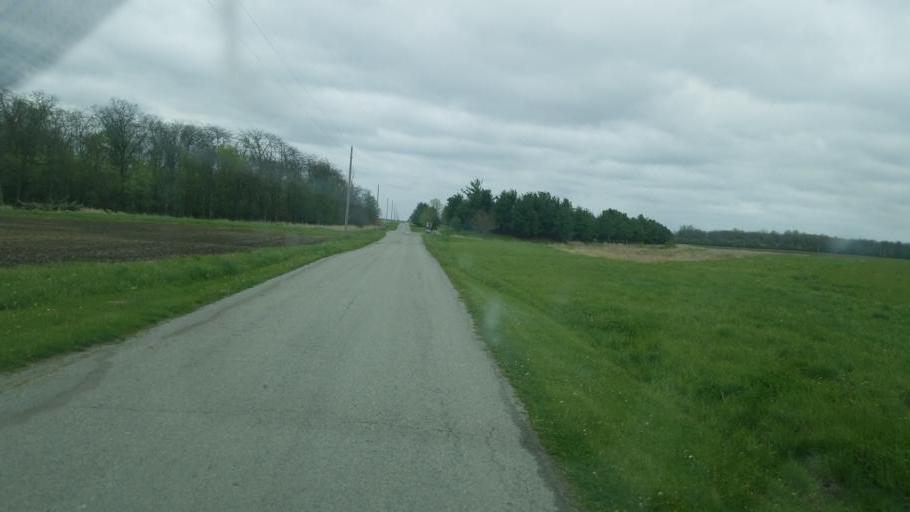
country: US
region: Ohio
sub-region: Hardin County
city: Kenton
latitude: 40.7247
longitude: -83.5951
